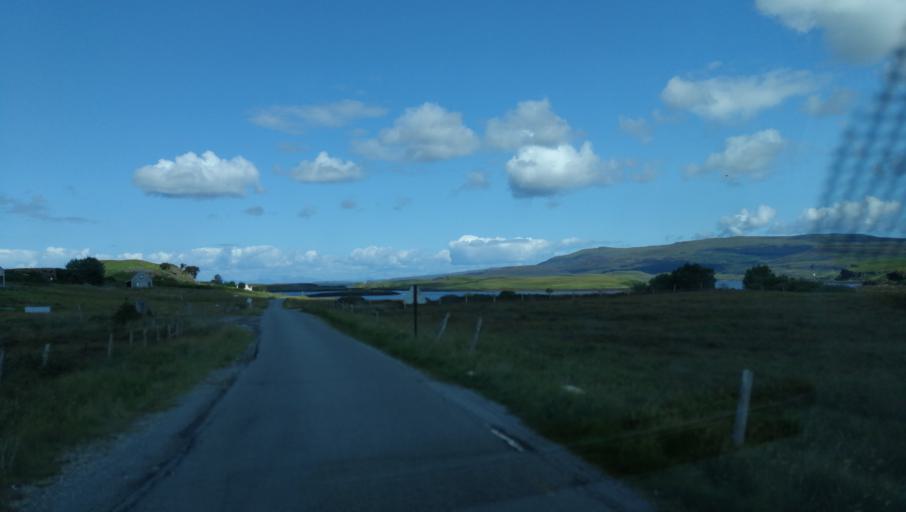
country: GB
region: Scotland
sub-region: Highland
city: Isle of Skye
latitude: 57.4319
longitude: -6.6246
